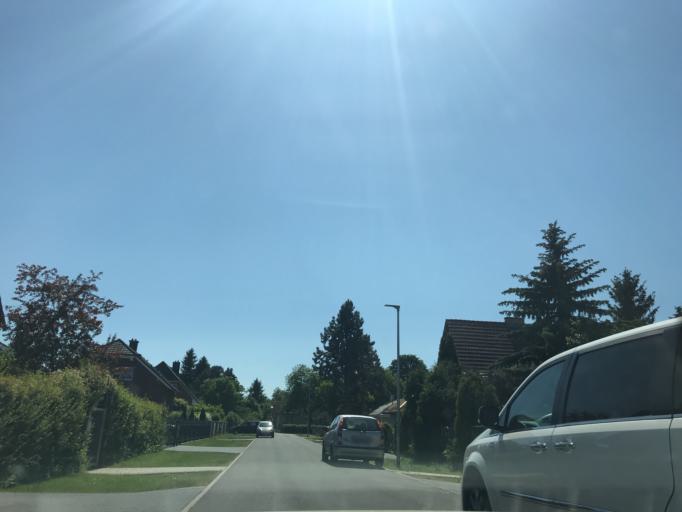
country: DE
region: Brandenburg
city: Falkensee
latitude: 52.5541
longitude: 13.0777
